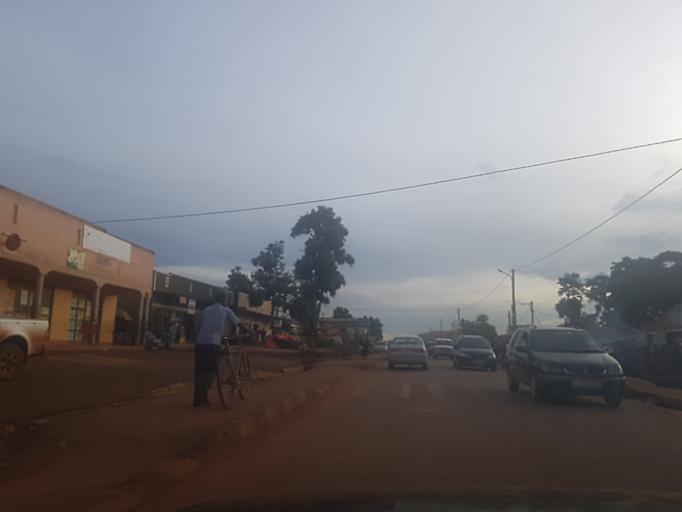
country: UG
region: Central Region
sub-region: Wakiso District
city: Bweyogerere
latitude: 0.3910
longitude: 32.6586
